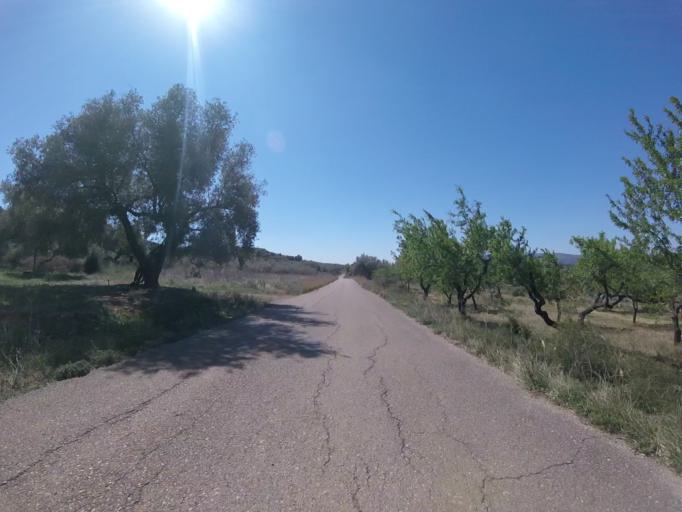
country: ES
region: Valencia
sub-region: Provincia de Castello
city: Cuevas de Vinroma
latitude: 40.3893
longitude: 0.1601
